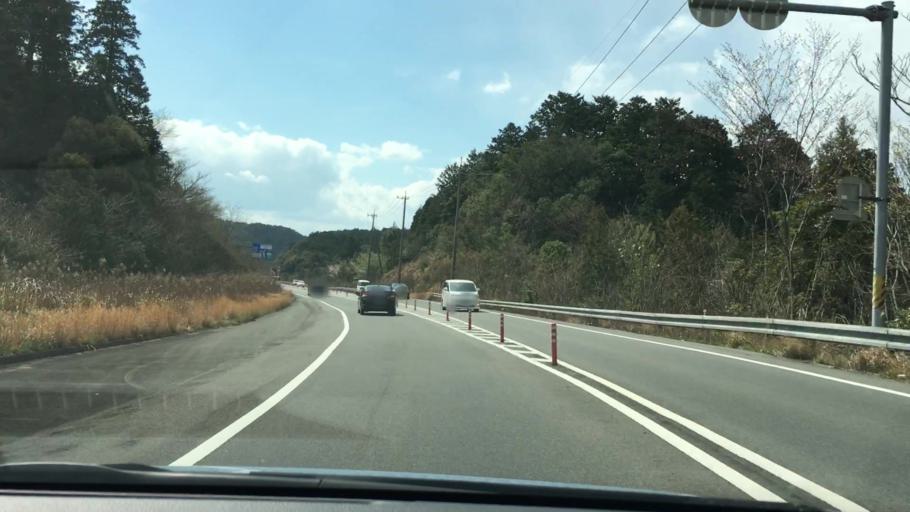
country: JP
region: Mie
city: Toba
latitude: 34.4902
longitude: 136.8094
